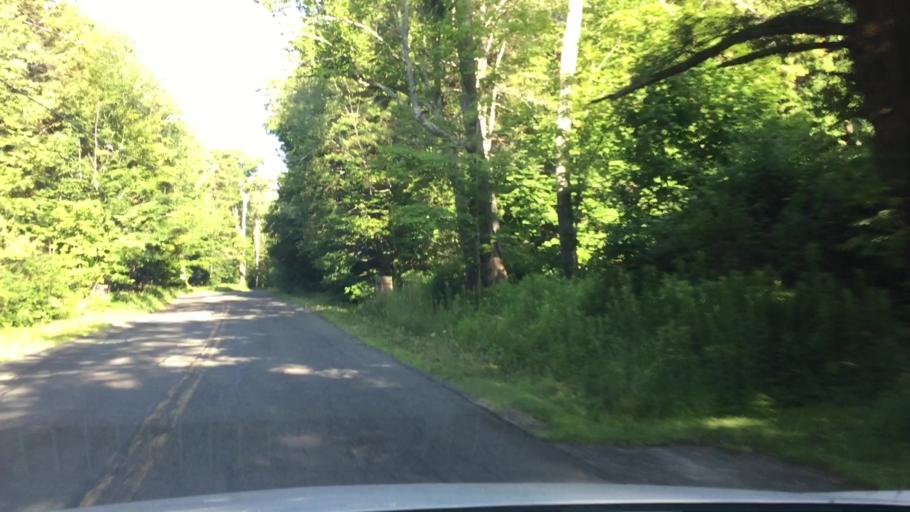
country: US
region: Massachusetts
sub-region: Berkshire County
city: Becket
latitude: 42.3168
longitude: -73.1062
